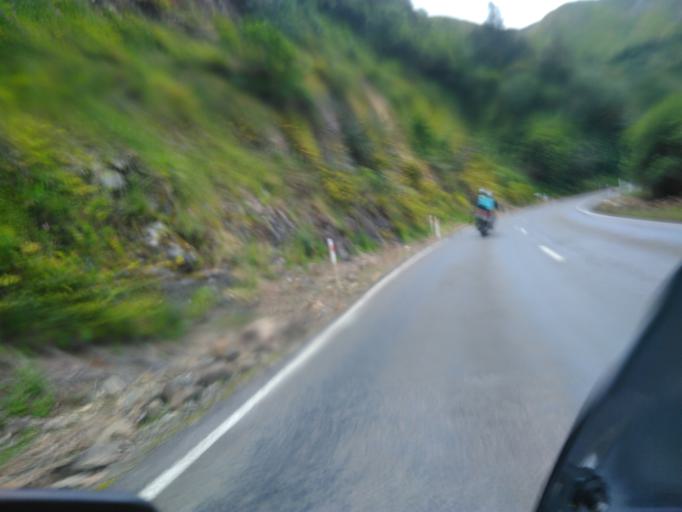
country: NZ
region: Bay of Plenty
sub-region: Opotiki District
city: Opotiki
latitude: -38.2676
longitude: 177.3062
